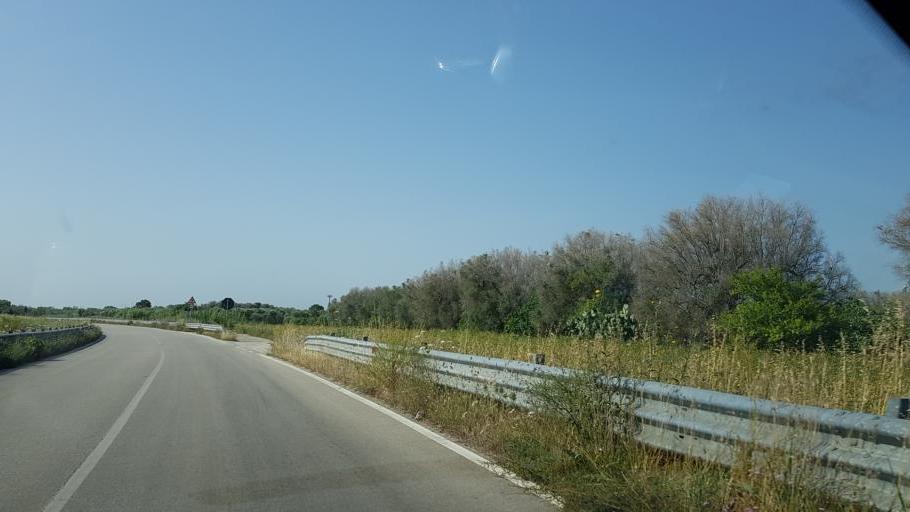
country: IT
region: Apulia
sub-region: Provincia di Brindisi
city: Mesagne
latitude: 40.4975
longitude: 17.8291
